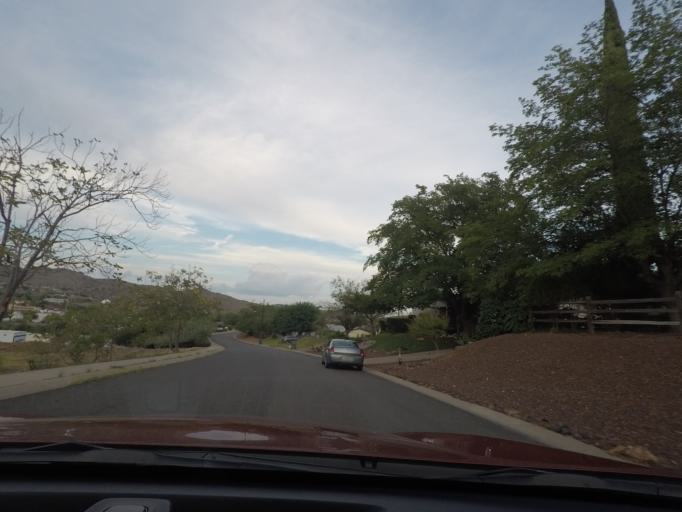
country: US
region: Arizona
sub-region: Yavapai County
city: Bagdad
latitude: 34.5718
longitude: -113.1825
